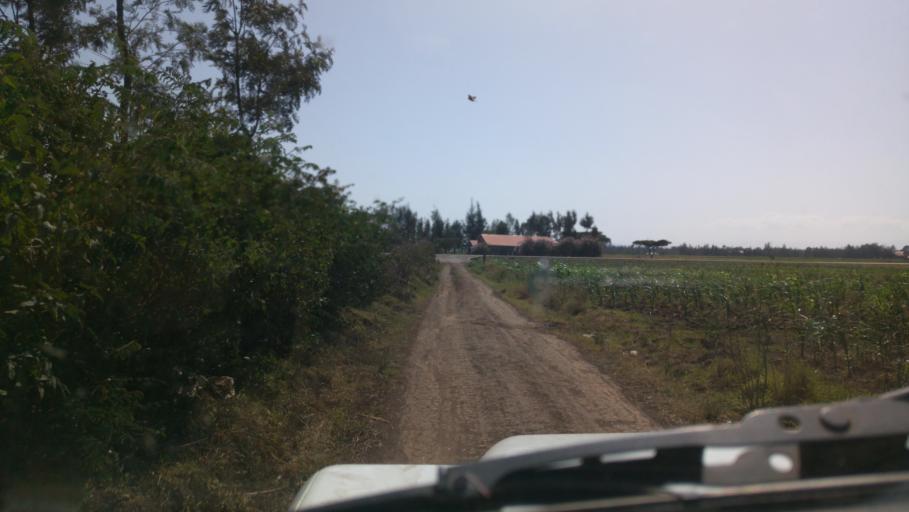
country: KE
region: Nakuru
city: Rongai
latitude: -0.2452
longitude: 35.9261
